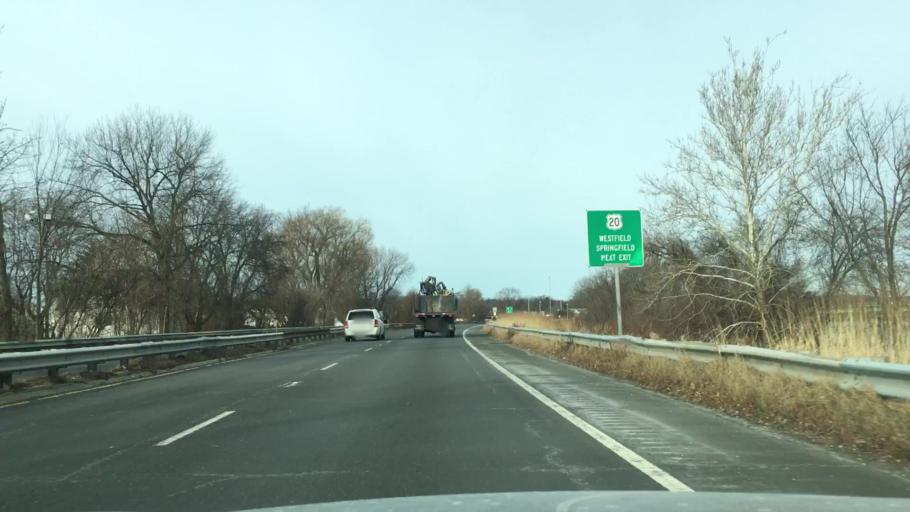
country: US
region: Massachusetts
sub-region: Hampden County
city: West Springfield
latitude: 42.1040
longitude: -72.6101
